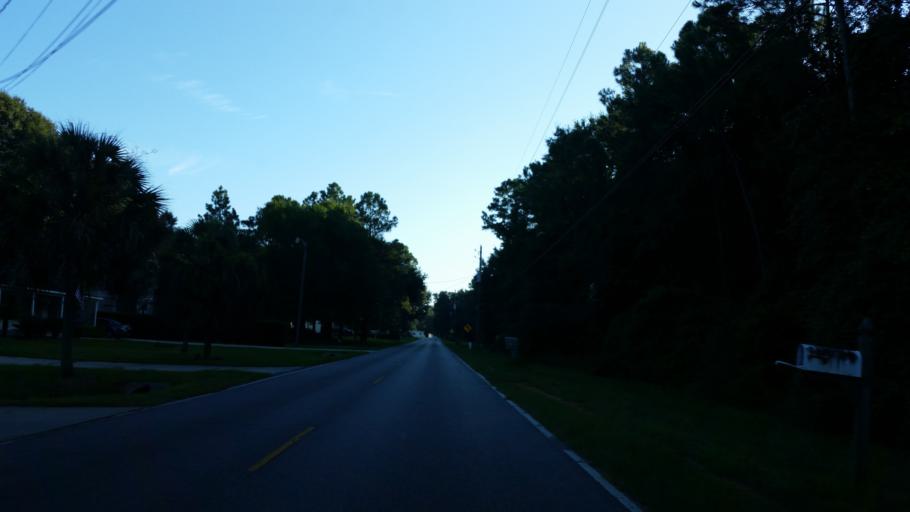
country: US
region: Florida
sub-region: Escambia County
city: Bellview
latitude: 30.4960
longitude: -87.3242
